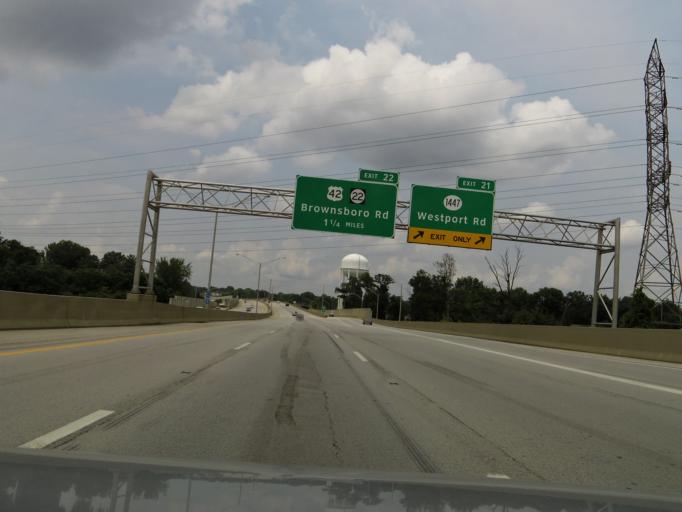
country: US
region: Kentucky
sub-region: Jefferson County
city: Beechwood Village
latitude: 38.2609
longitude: -85.6231
